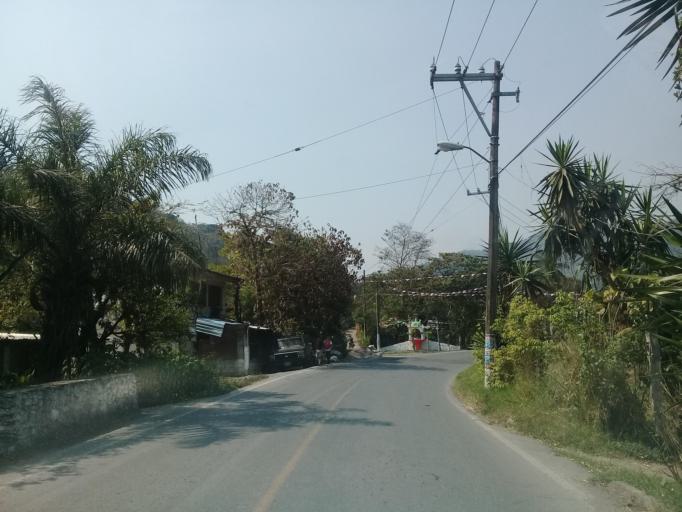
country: MX
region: Veracruz
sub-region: Ixtaczoquitlan
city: Campo Chico
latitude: 18.8266
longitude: -97.0209
